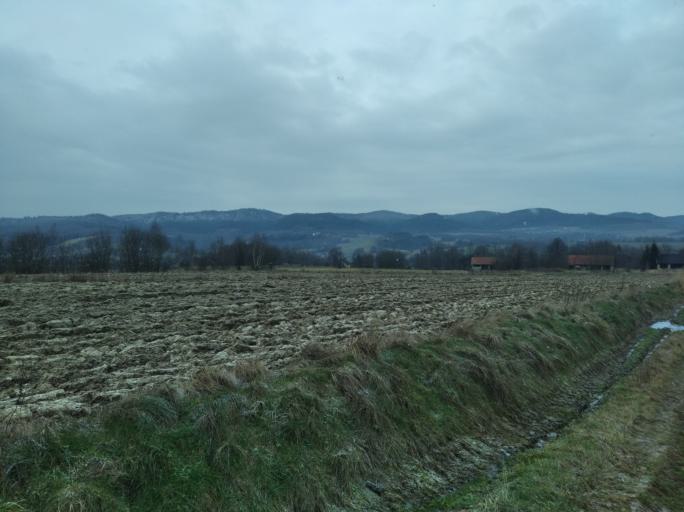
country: PL
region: Subcarpathian Voivodeship
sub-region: Powiat strzyzowski
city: Wysoka Strzyzowska
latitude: 49.8325
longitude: 21.7553
